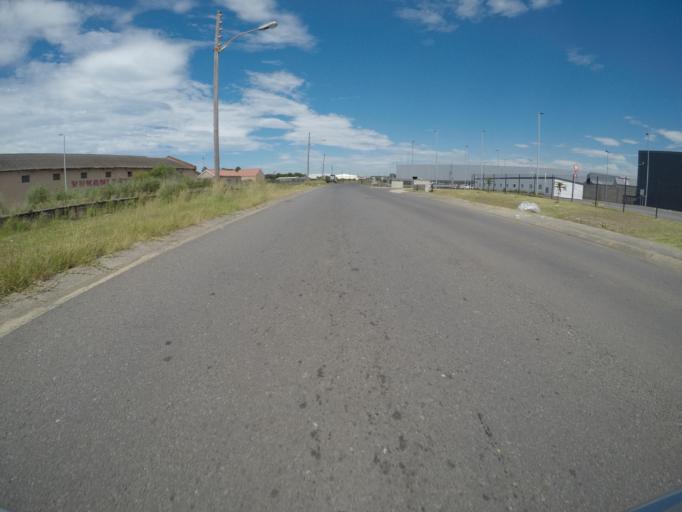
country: ZA
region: Eastern Cape
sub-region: Buffalo City Metropolitan Municipality
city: East London
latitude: -33.0325
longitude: 27.8939
